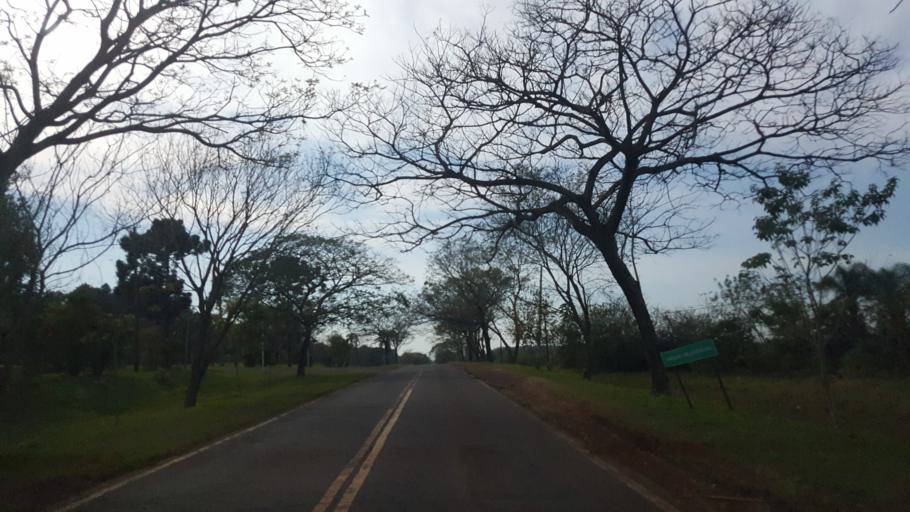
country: AR
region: Misiones
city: Capiovi
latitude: -26.9334
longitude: -55.1082
